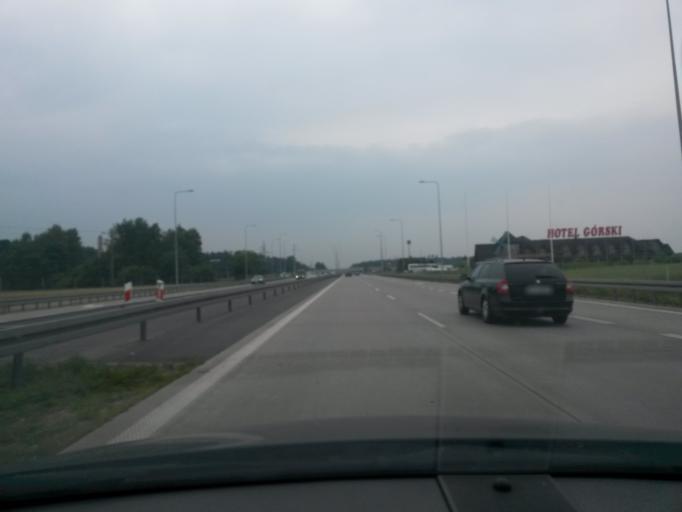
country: PL
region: Lodz Voivodeship
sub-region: Powiat piotrkowski
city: Wolborz
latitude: 51.4624
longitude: 19.7841
